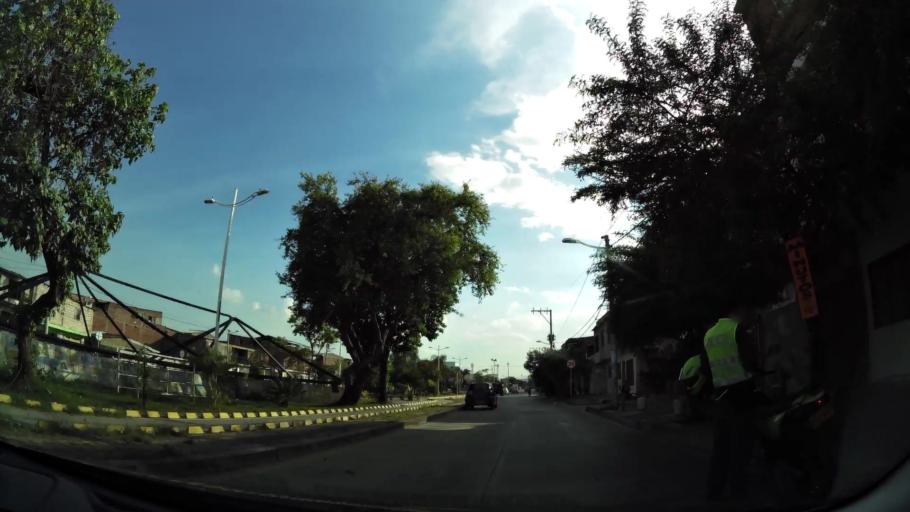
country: CO
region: Valle del Cauca
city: Cali
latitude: 3.4228
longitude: -76.4893
